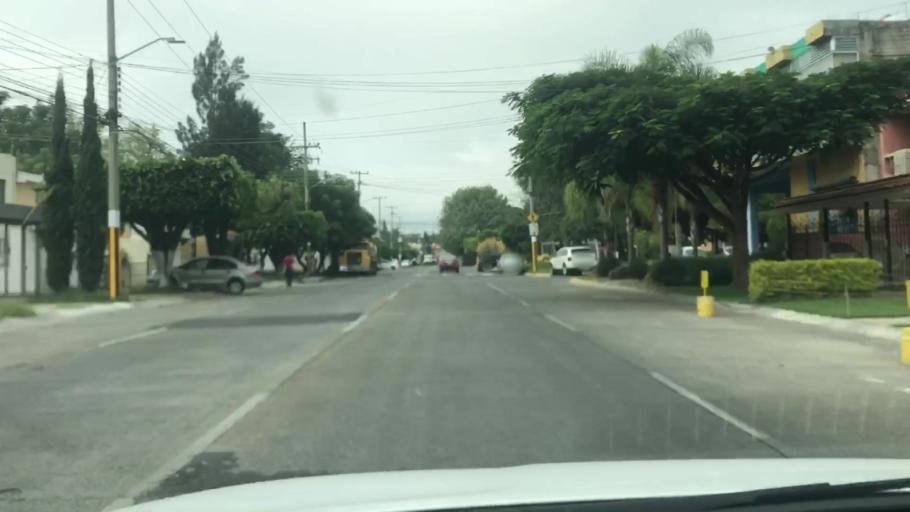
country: MX
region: Jalisco
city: Guadalajara
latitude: 20.6355
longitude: -103.4294
